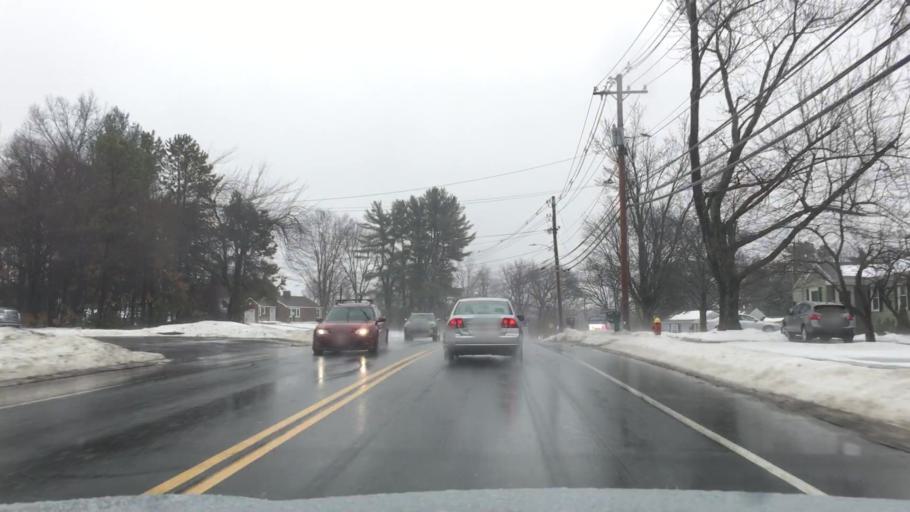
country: US
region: Massachusetts
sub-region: Hampden County
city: Ludlow
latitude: 42.1733
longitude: -72.5362
